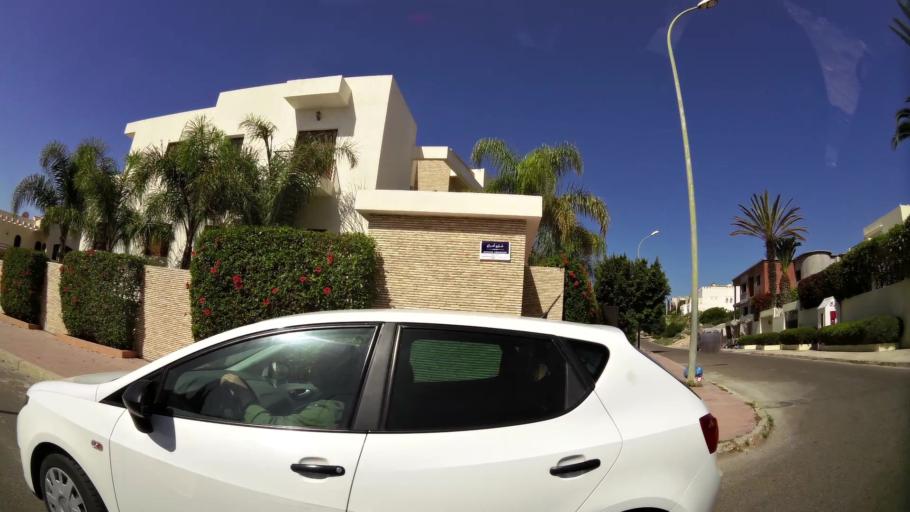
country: MA
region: Souss-Massa-Draa
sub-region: Agadir-Ida-ou-Tnan
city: Agadir
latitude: 30.4429
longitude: -9.5812
